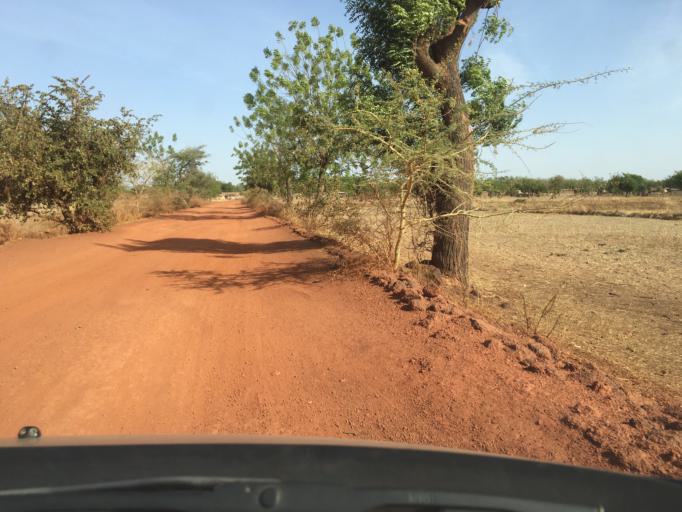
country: BF
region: Plateau-Central
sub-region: Province du Kourweogo
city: Bousse
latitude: 12.5723
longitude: -1.9287
